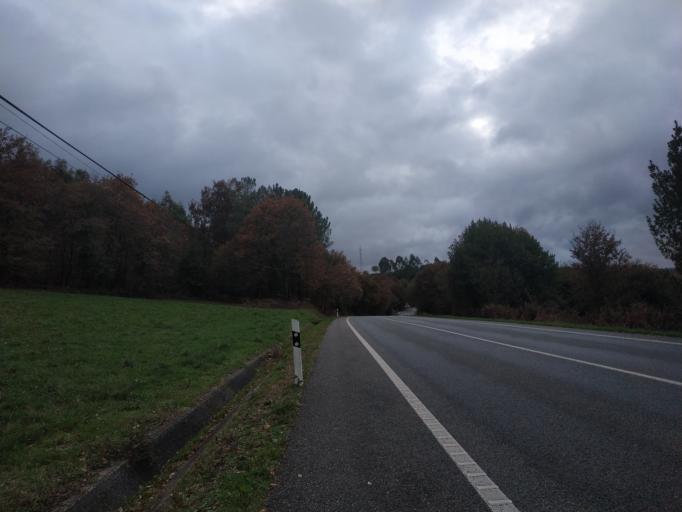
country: ES
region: Galicia
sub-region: Provincia de Pontevedra
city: Silleda
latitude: 42.7796
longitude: -8.1738
